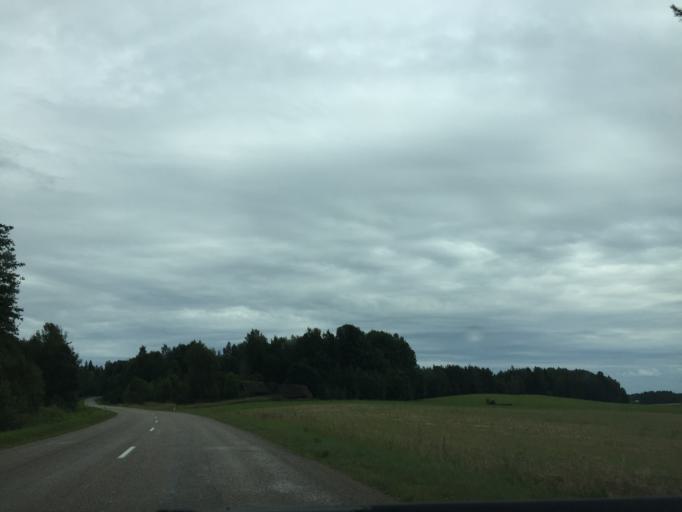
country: LV
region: Dagda
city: Dagda
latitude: 56.1867
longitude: 27.3601
